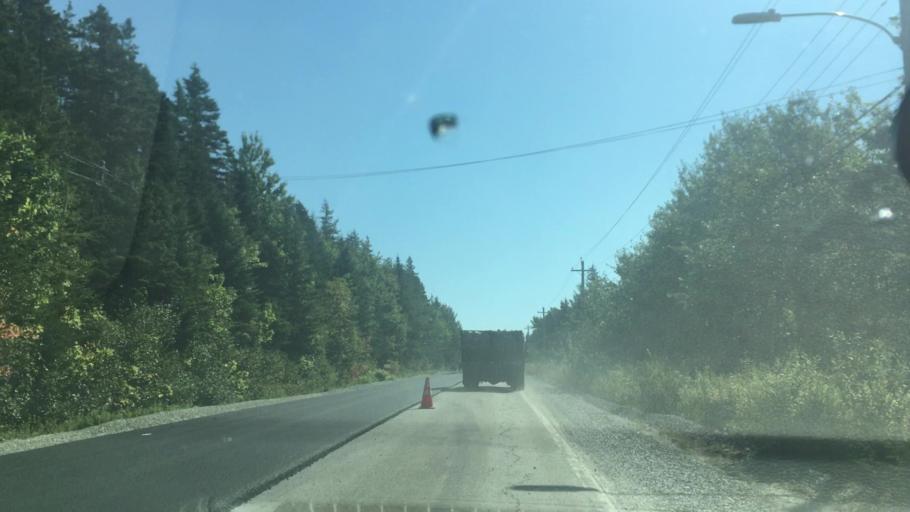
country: CA
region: Nova Scotia
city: New Glasgow
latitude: 44.9100
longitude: -62.5035
